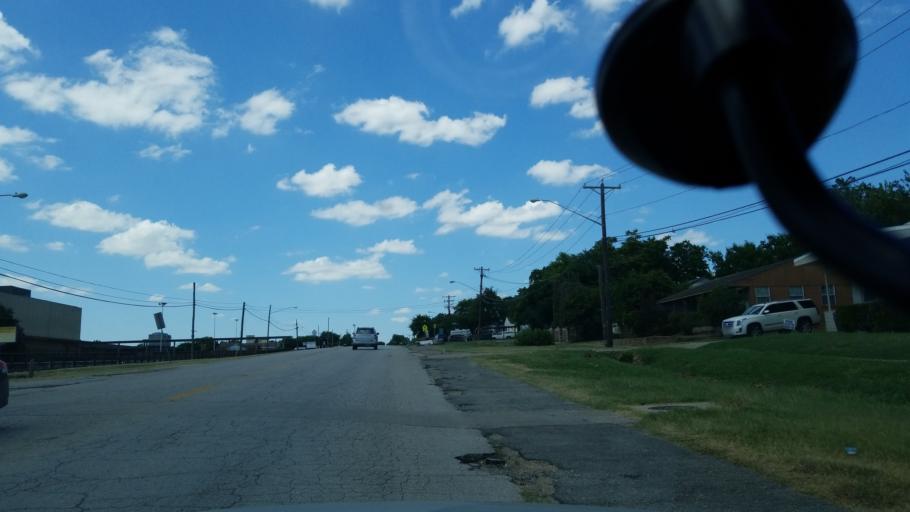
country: US
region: Texas
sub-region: Dallas County
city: Cockrell Hill
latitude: 32.7020
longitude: -96.8229
